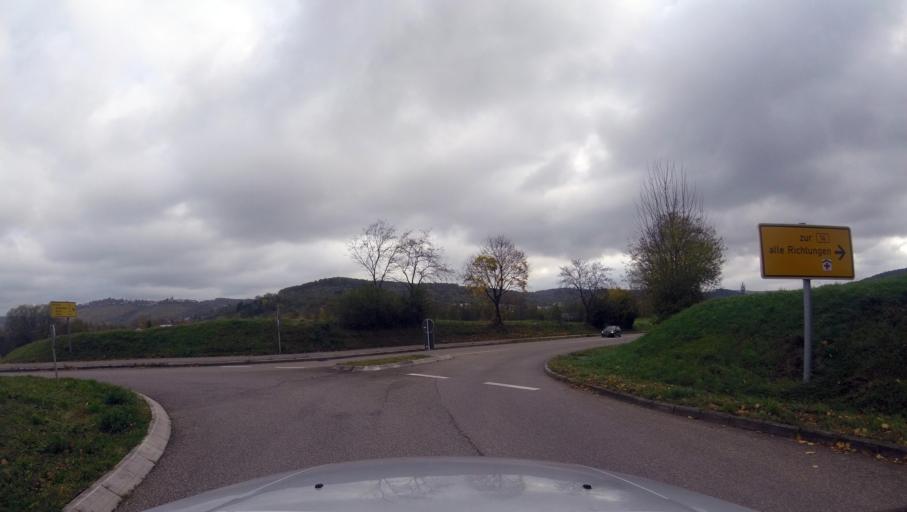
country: DE
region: Baden-Wuerttemberg
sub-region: Regierungsbezirk Stuttgart
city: Winnenden
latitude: 48.8698
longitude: 9.4190
